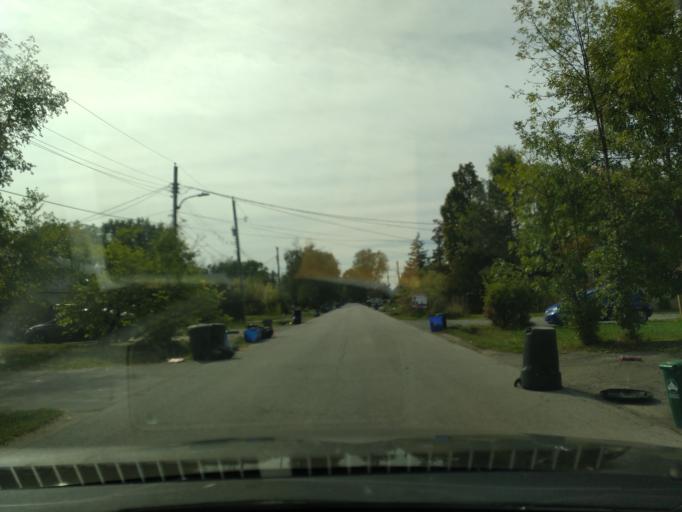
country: CA
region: Ontario
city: Keswick
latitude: 44.2161
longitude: -79.4686
